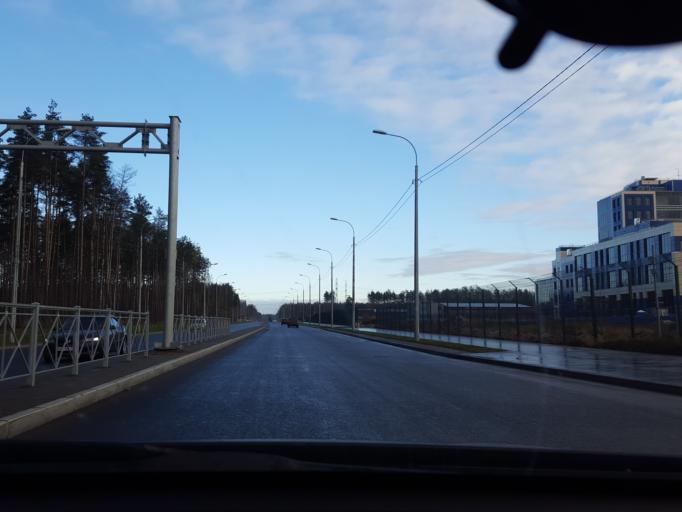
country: RU
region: Leningrad
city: Untolovo
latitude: 60.0532
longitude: 30.2282
